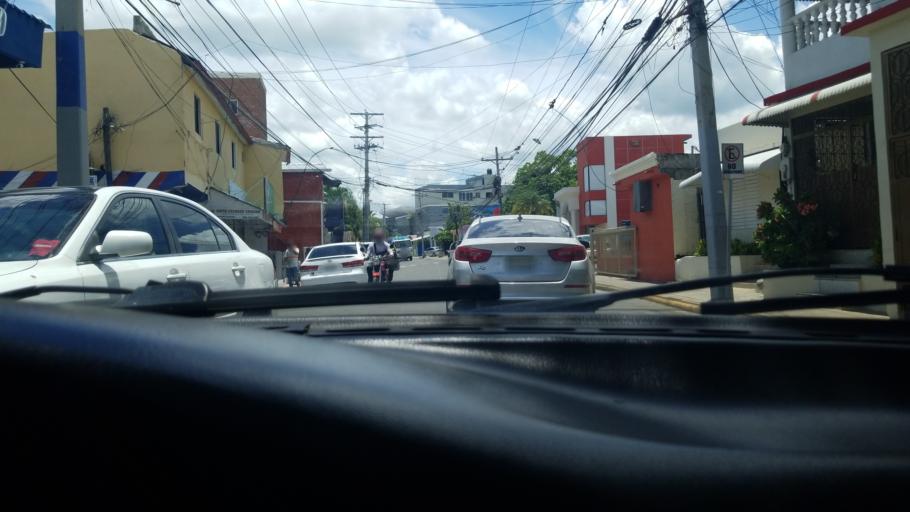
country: DO
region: Santiago
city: Santiago de los Caballeros
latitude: 19.4744
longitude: -70.6864
